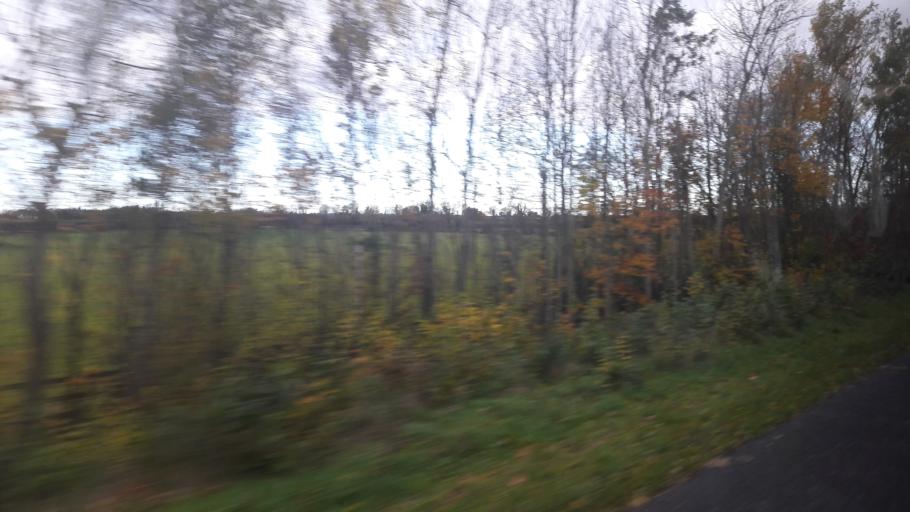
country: IE
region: Leinster
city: Balrothery
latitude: 53.5877
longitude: -6.2125
